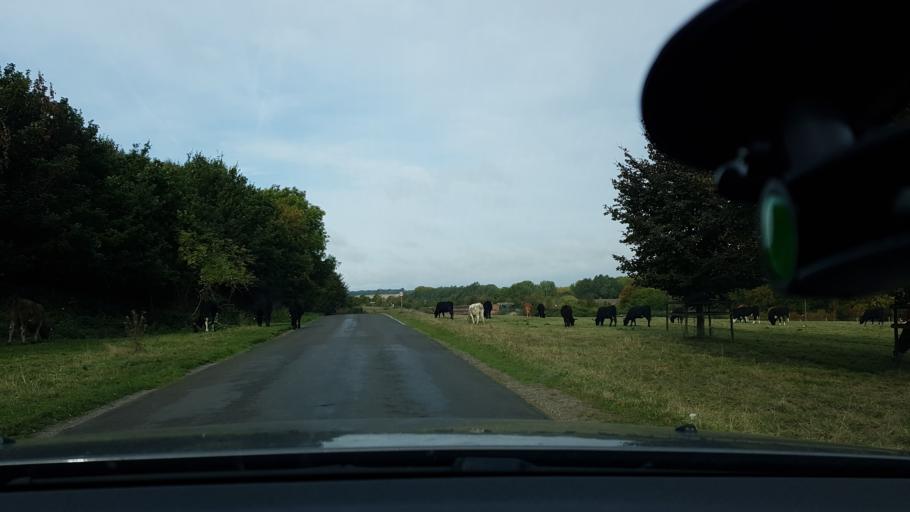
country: GB
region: England
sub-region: West Berkshire
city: Hungerford
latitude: 51.4100
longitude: -1.4939
